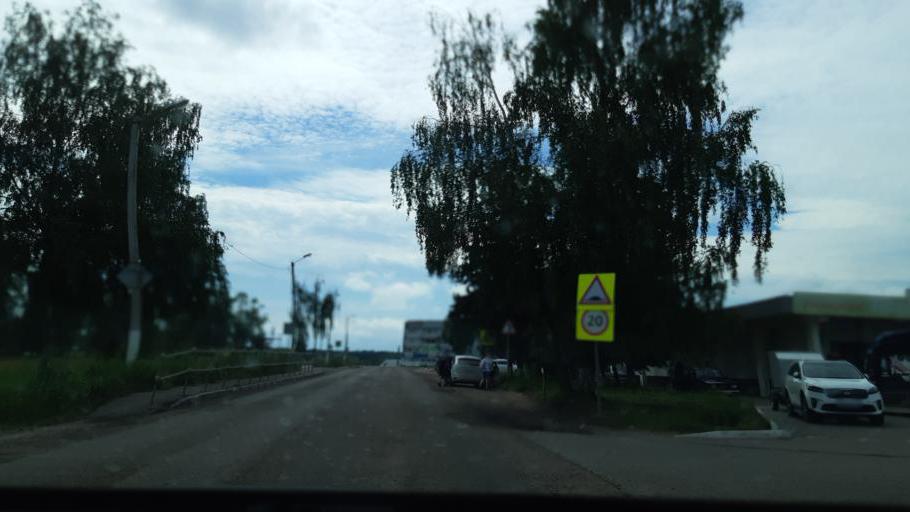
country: RU
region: Moskovskaya
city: Vereya
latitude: 55.3020
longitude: 36.0953
